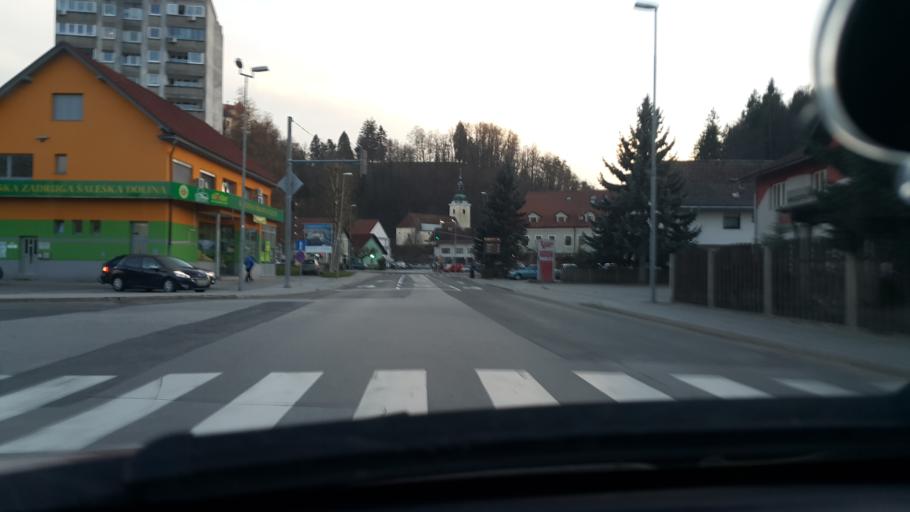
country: SI
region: Velenje
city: Velenje
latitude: 46.3598
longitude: 15.1077
